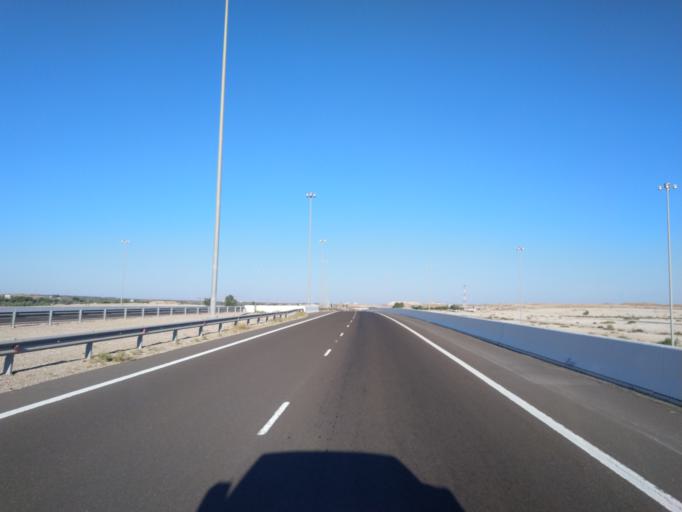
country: OM
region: Al Buraimi
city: Al Buraymi
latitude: 24.5257
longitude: 55.5516
